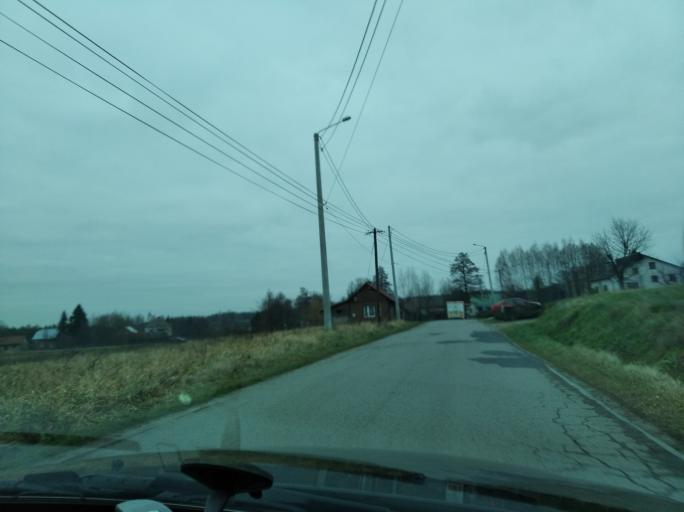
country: PL
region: Subcarpathian Voivodeship
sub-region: Powiat lancucki
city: Brzoza Stadnicka
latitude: 50.2038
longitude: 22.2972
